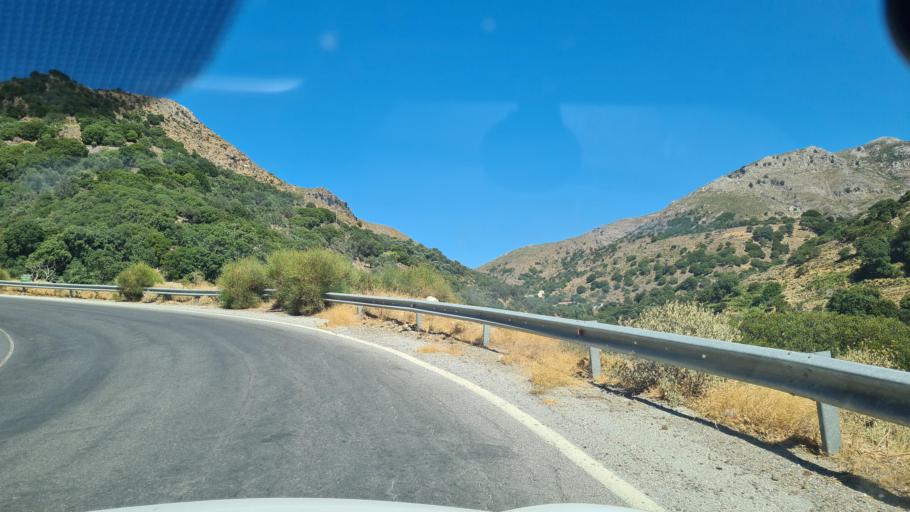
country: GR
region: Crete
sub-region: Nomos Chanias
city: Vryses
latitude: 35.3615
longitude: 23.6023
